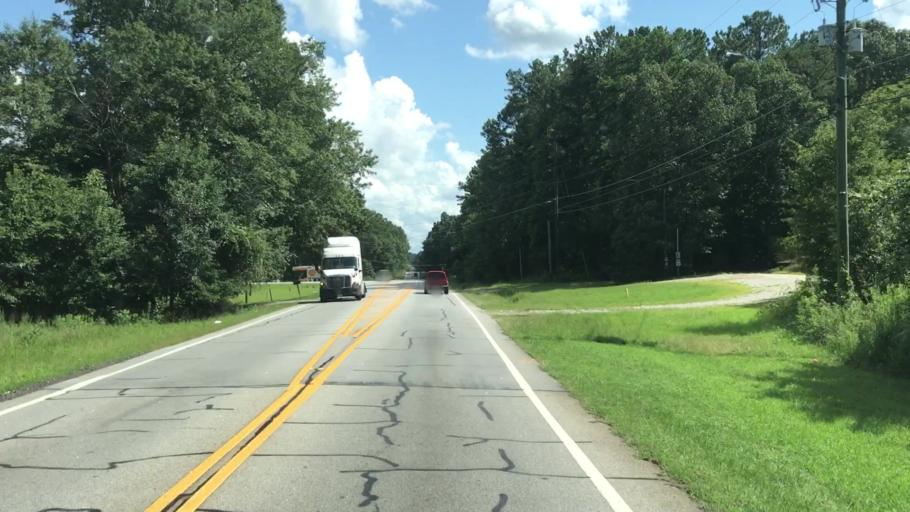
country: US
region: Georgia
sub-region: Walton County
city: Walnut Grove
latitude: 33.7215
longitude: -83.8525
